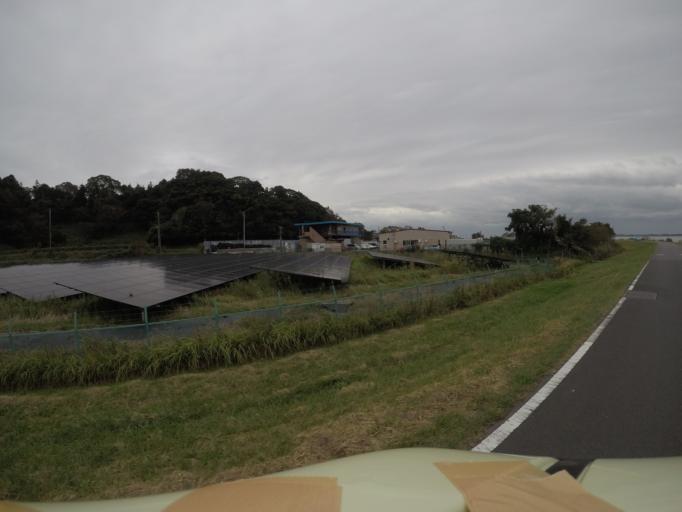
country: JP
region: Ibaraki
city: Ami
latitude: 36.0627
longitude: 140.2893
